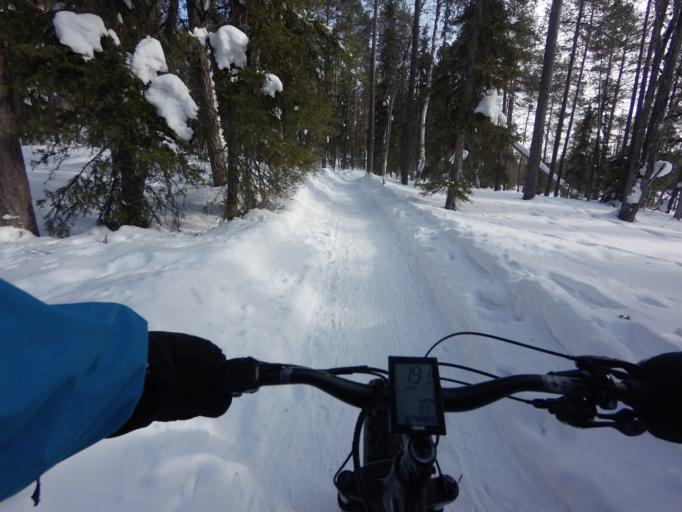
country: FI
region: Lapland
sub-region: Tunturi-Lappi
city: Kolari
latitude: 67.6008
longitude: 24.2430
